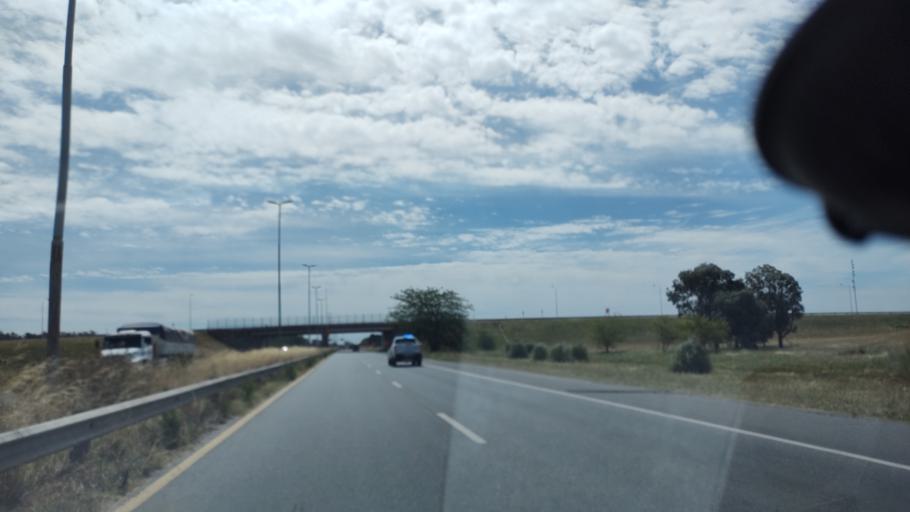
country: AR
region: Buenos Aires
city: Canuelas
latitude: -35.0223
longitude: -58.7406
